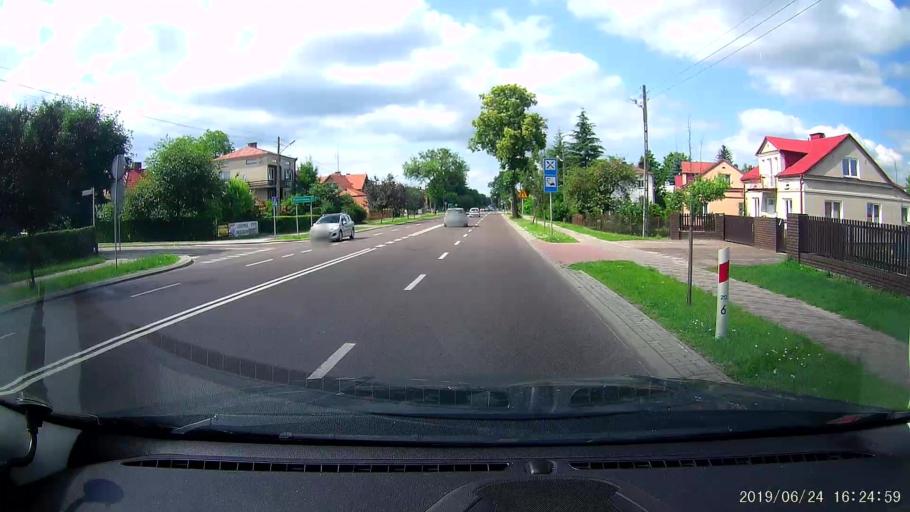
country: PL
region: Lublin Voivodeship
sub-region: Powiat tomaszowski
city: Tomaszow Lubelski
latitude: 50.4402
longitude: 23.4187
